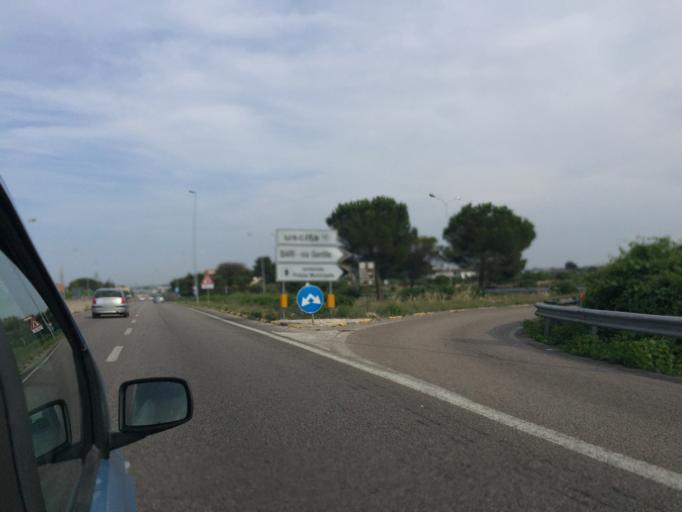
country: IT
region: Apulia
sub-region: Provincia di Bari
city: Triggiano
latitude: 41.1006
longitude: 16.9301
